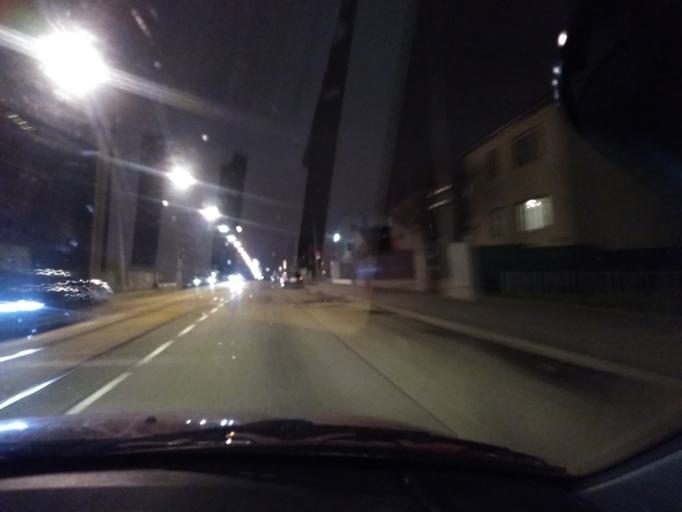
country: AT
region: Lower Austria
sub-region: Politischer Bezirk Modling
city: Perchtoldsdorf
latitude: 48.1586
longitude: 16.2755
